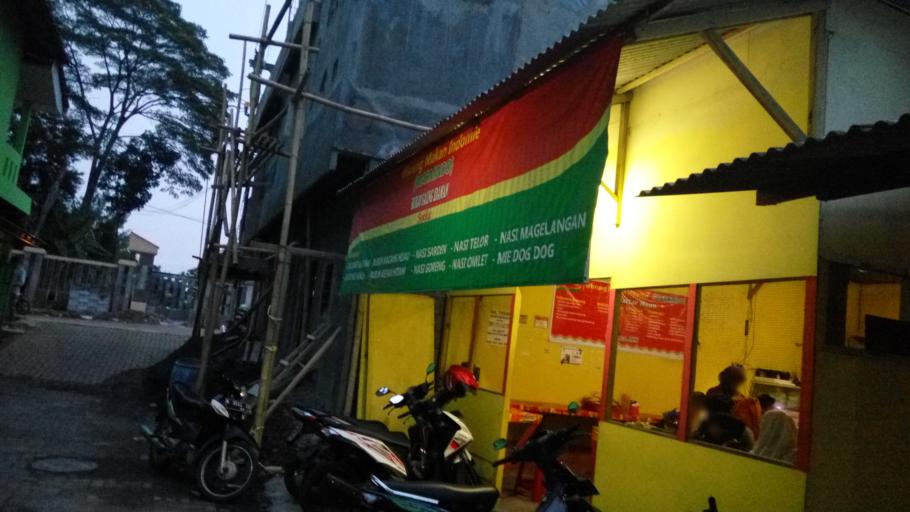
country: ID
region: Central Java
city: Semarang
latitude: -7.0510
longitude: 110.4444
